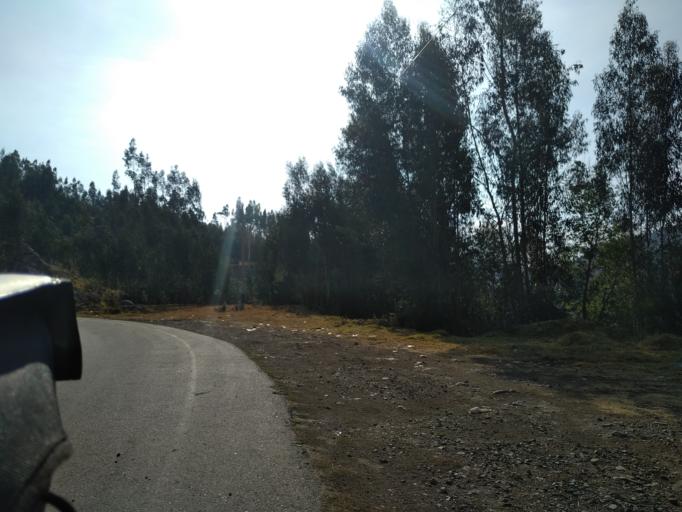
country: PE
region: La Libertad
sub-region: Provincia de Otuzco
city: Agallpampa
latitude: -7.9952
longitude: -78.5131
